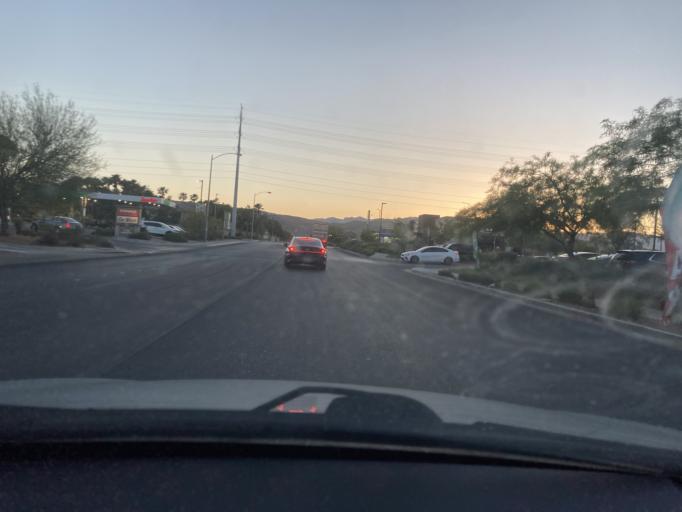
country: US
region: Nevada
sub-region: Clark County
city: Enterprise
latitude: 36.0593
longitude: -115.2777
